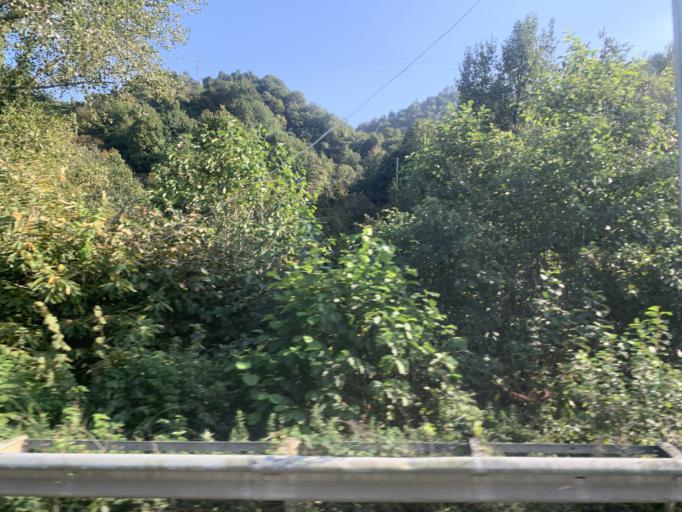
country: TR
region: Trabzon
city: Of
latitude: 40.9347
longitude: 40.2448
